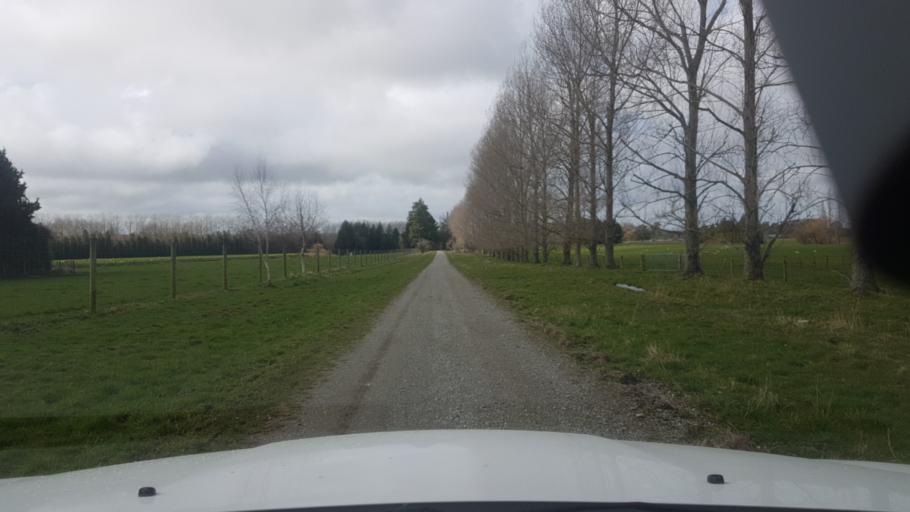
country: NZ
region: Canterbury
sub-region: Timaru District
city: Pleasant Point
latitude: -44.0111
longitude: 171.2075
